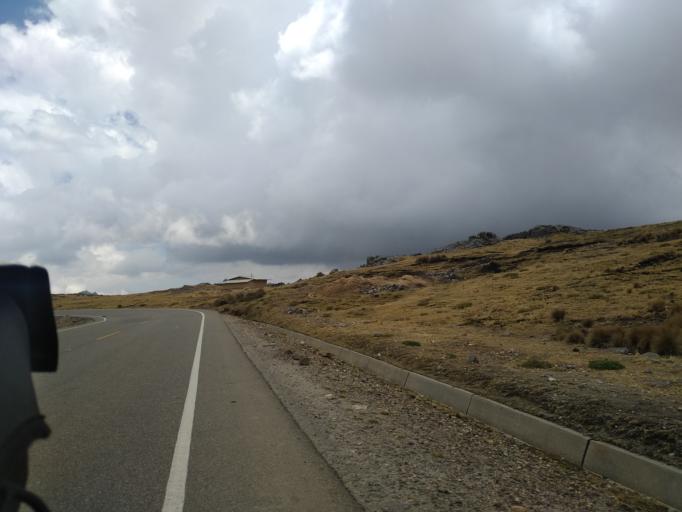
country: PE
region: La Libertad
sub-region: Provincia de Santiago de Chuco
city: Quiruvilca
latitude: -7.9680
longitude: -78.2019
